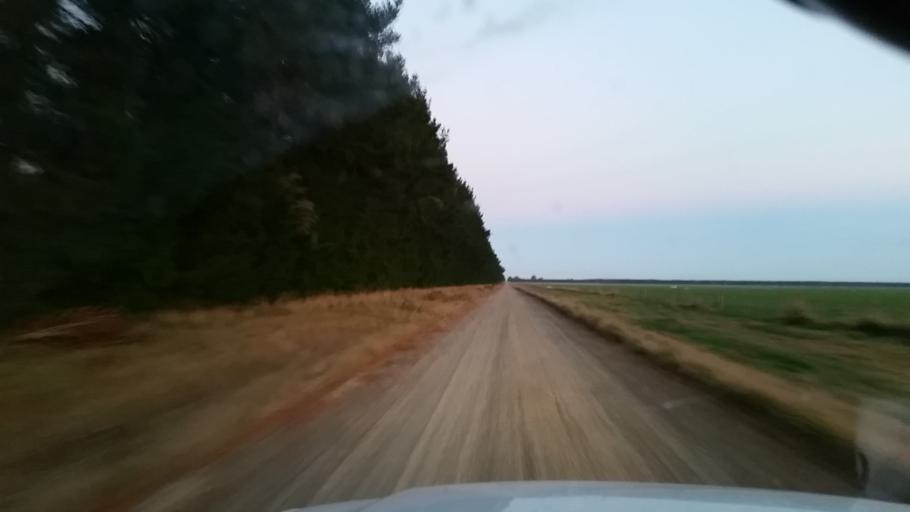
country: NZ
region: Canterbury
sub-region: Ashburton District
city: Tinwald
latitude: -43.9486
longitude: 171.6138
